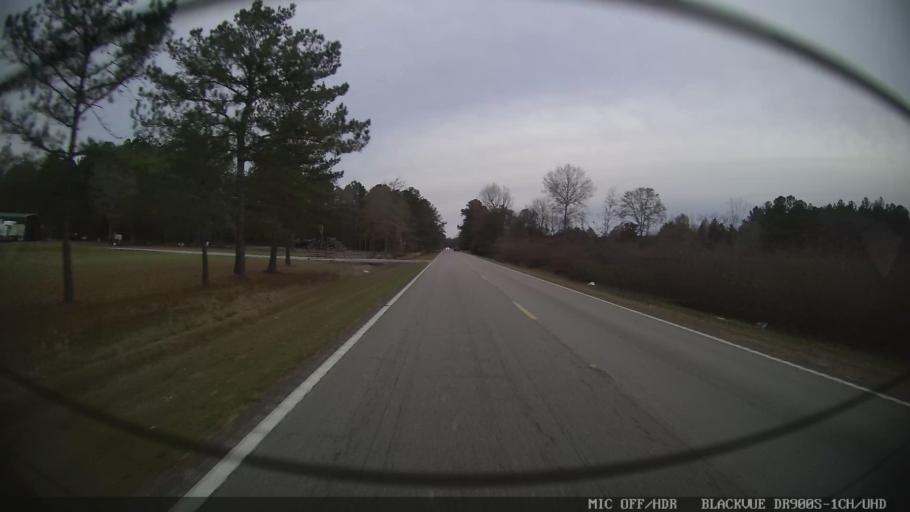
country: US
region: Mississippi
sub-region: Clarke County
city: Stonewall
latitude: 32.0346
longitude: -88.8730
